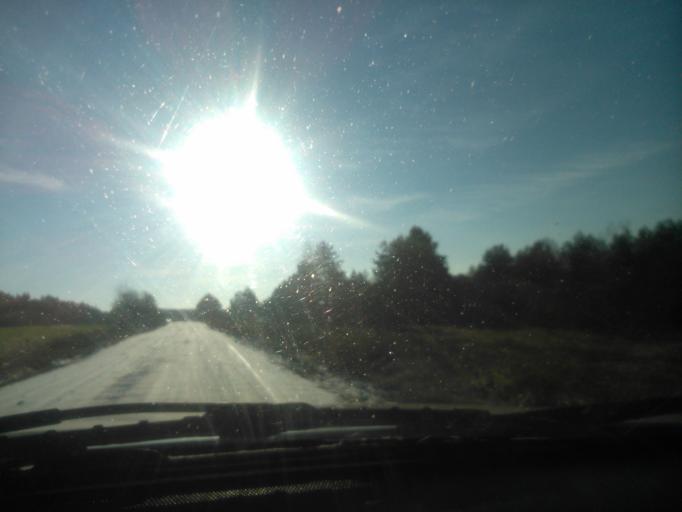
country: PL
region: Warmian-Masurian Voivodeship
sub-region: Powiat nowomiejski
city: Kurzetnik
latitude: 53.3710
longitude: 19.5303
